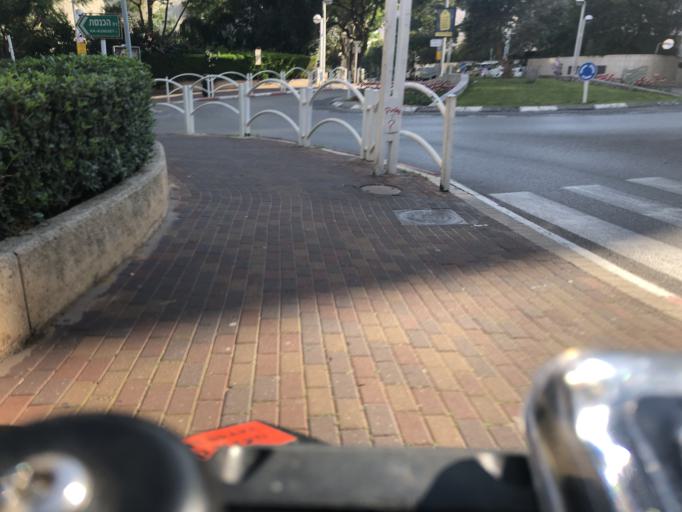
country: IL
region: Tel Aviv
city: Giv`atayim
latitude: 32.0674
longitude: 34.8121
